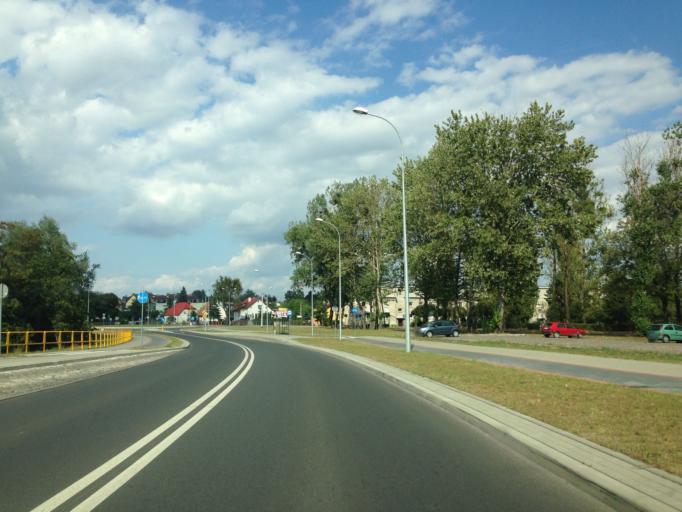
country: PL
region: Warmian-Masurian Voivodeship
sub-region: Powiat ilawski
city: Ilawa
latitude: 53.5829
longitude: 19.5699
